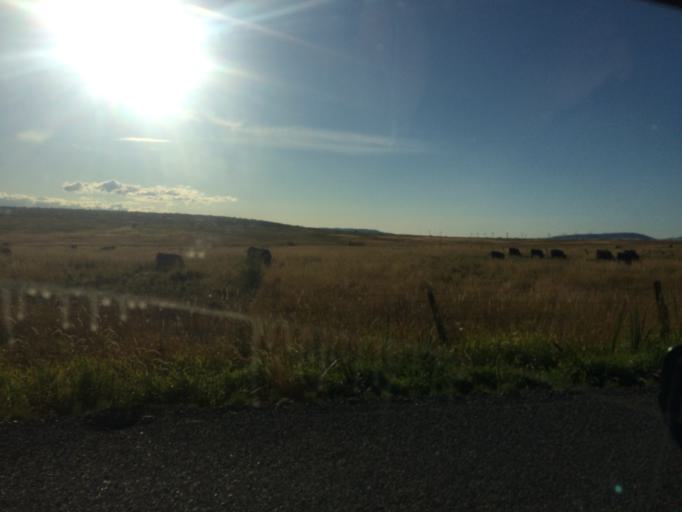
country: US
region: Washington
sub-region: Kittitas County
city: Ellensburg
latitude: 47.0820
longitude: -120.6031
